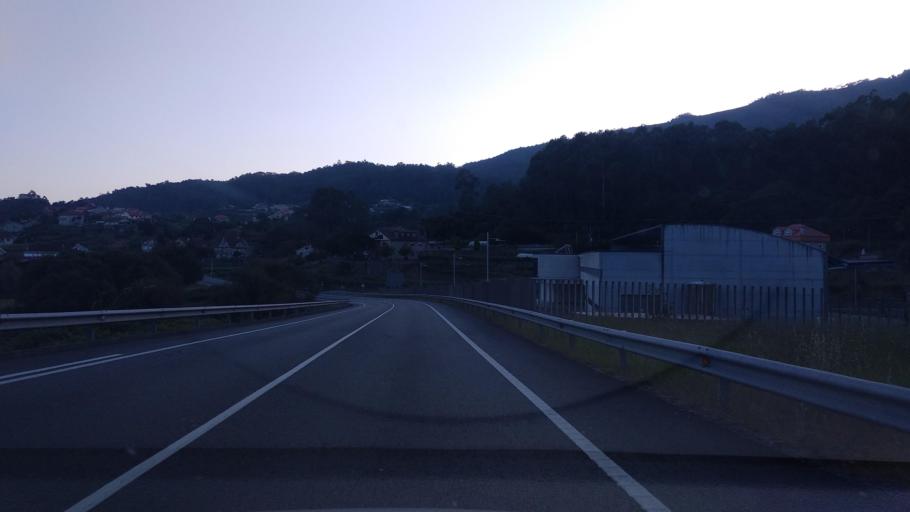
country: ES
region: Galicia
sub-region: Provincia de Pontevedra
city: Marin
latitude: 42.3542
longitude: -8.6392
